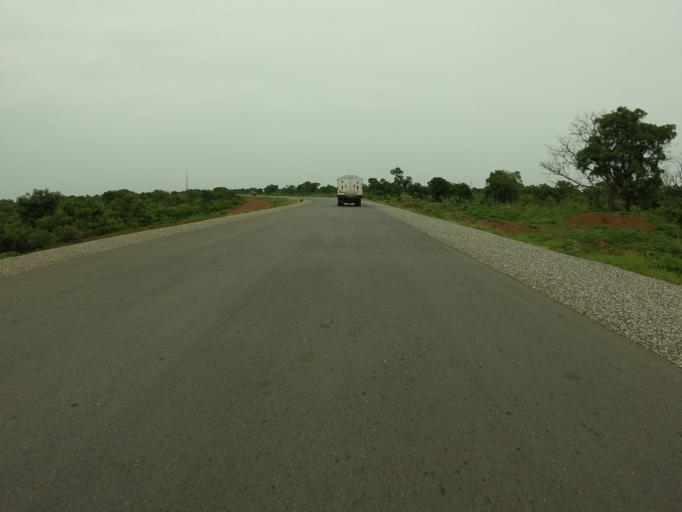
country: GH
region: Northern
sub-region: Yendi
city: Yendi
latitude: 9.2936
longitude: 0.0184
